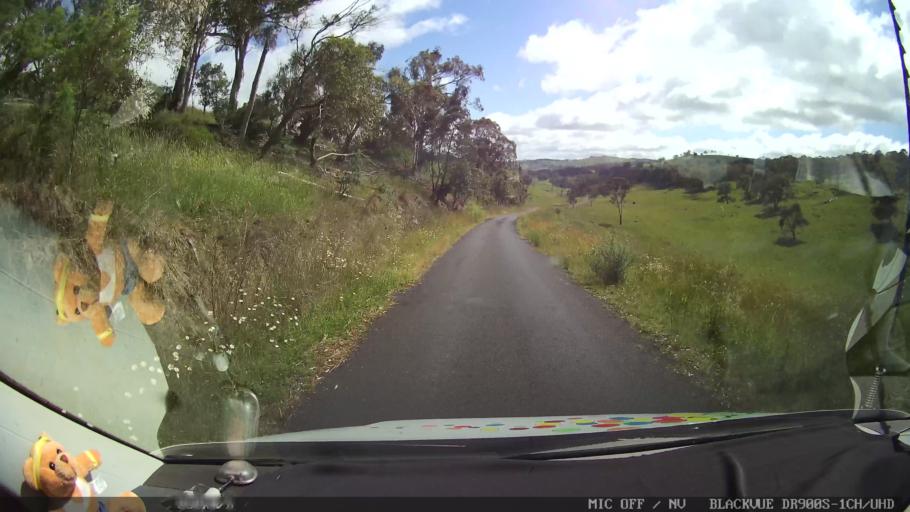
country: AU
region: New South Wales
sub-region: Guyra
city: Guyra
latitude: -30.0009
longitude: 151.6720
